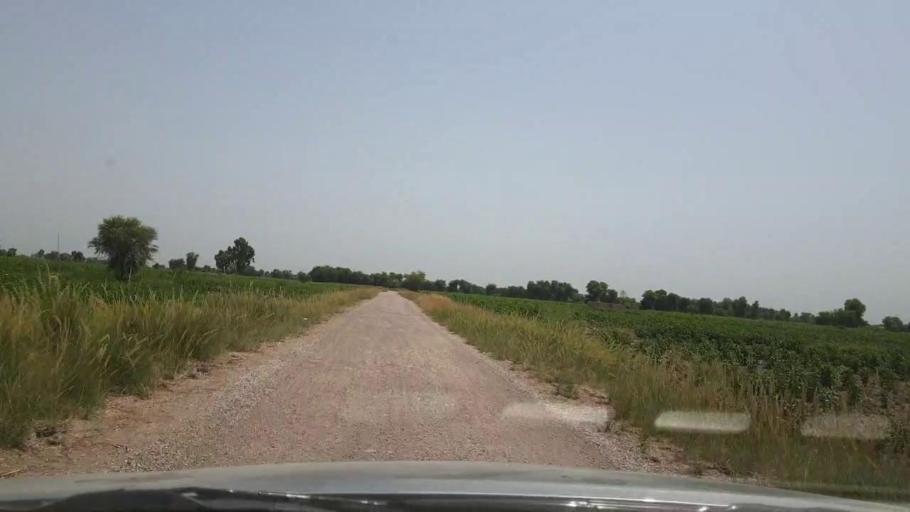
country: PK
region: Sindh
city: Pano Aqil
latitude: 27.8006
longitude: 69.2419
